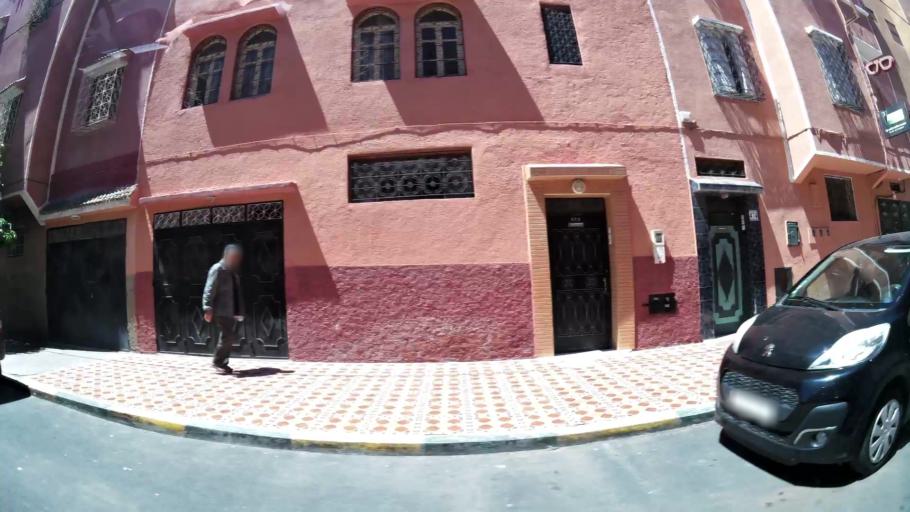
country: MA
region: Marrakech-Tensift-Al Haouz
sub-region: Marrakech
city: Marrakesh
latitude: 31.6317
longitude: -8.0532
